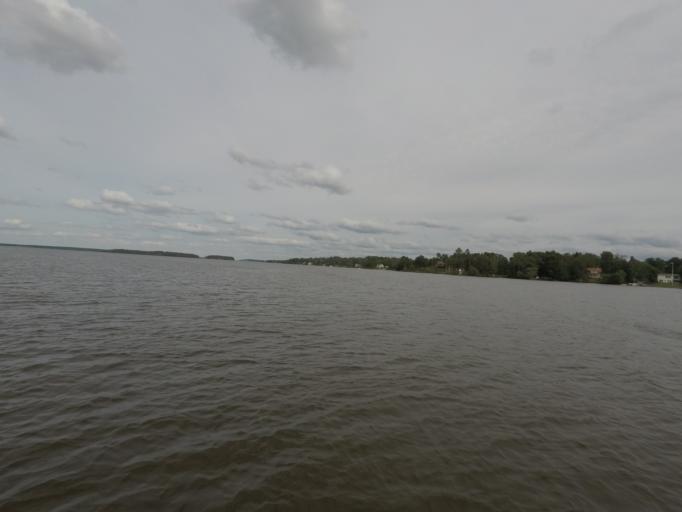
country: SE
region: Soedermanland
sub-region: Eskilstuna Kommun
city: Kvicksund
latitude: 59.4542
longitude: 16.3250
